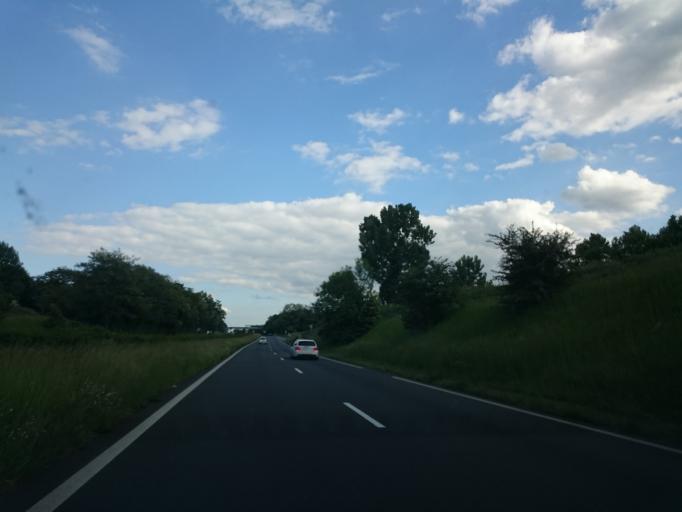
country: FR
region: Ile-de-France
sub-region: Departement de l'Essonne
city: Evry
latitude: 48.6325
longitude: 2.4375
